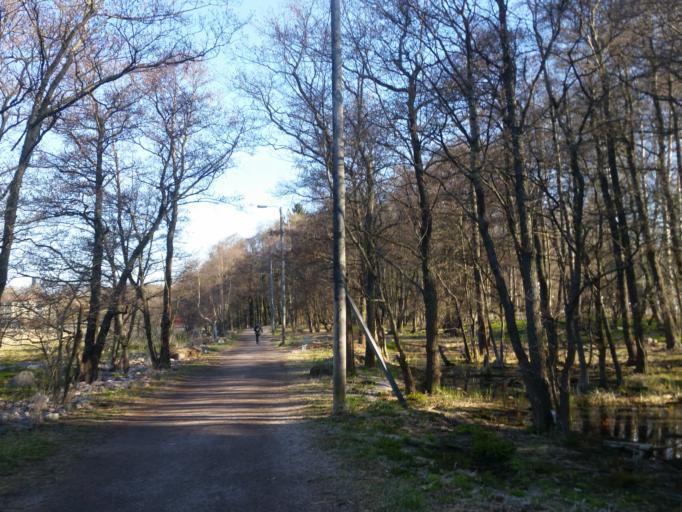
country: FI
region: Uusimaa
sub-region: Helsinki
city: Teekkarikylae
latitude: 60.1519
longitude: 24.8750
